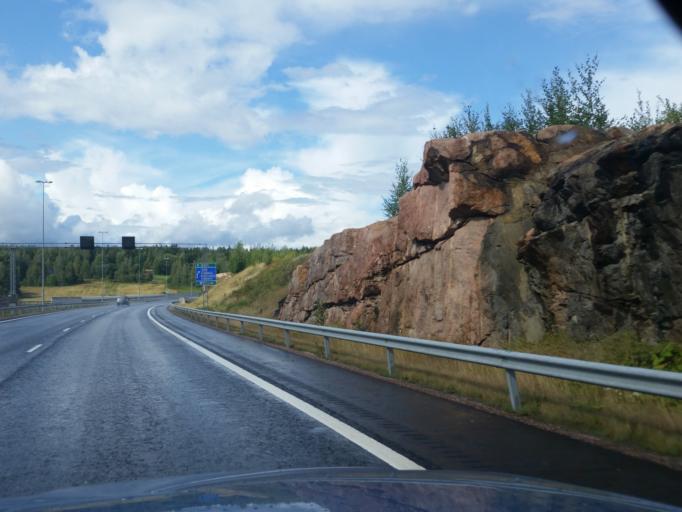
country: FI
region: Uusimaa
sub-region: Helsinki
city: Saukkola
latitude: 60.3281
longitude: 23.9373
